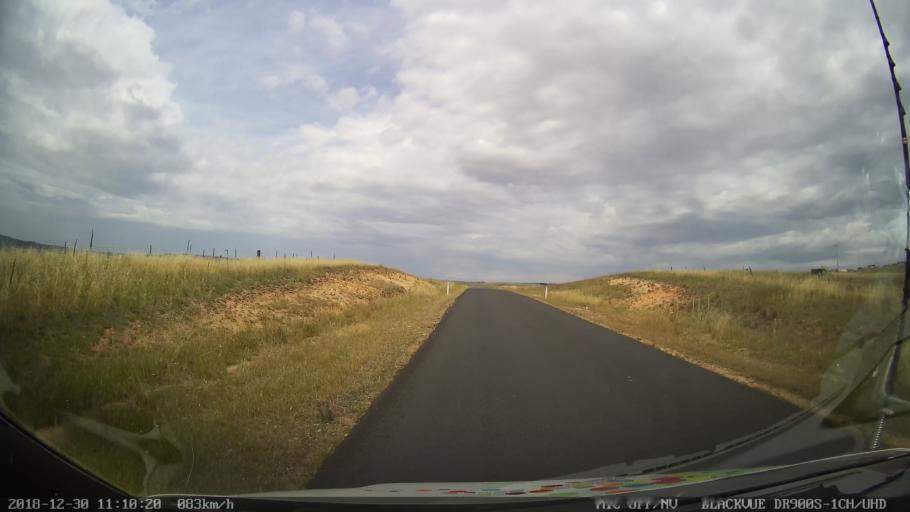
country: AU
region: New South Wales
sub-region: Snowy River
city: Berridale
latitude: -36.5139
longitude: 148.7825
